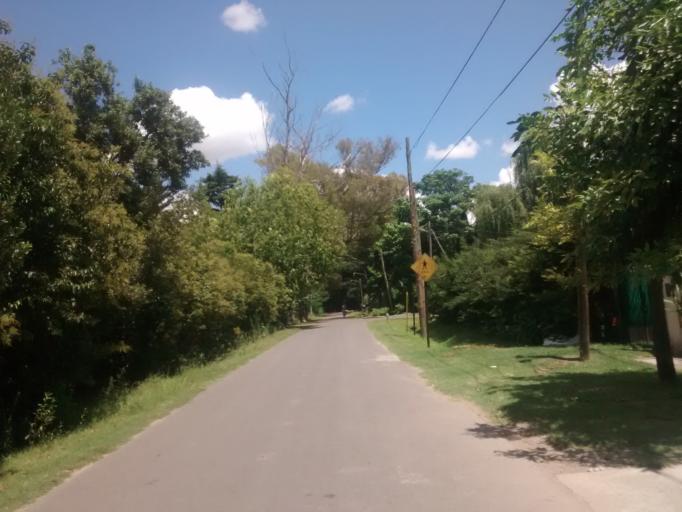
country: AR
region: Buenos Aires
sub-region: Partido de La Plata
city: La Plata
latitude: -34.8590
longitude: -58.0748
